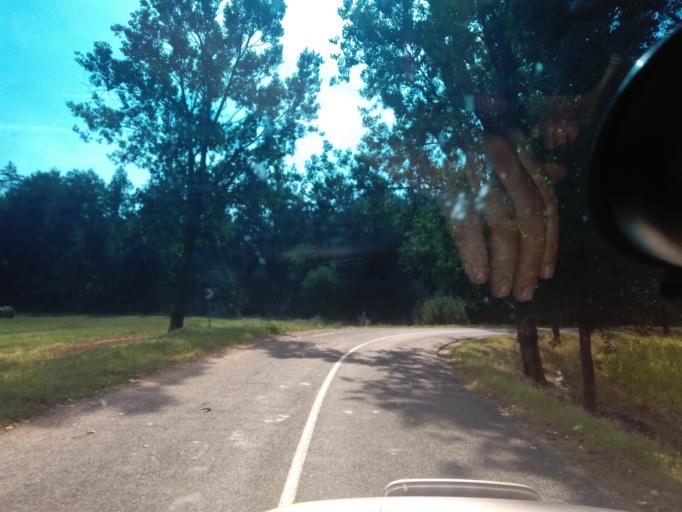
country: BY
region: Minsk
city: Kapyl'
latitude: 53.2748
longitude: 27.2307
